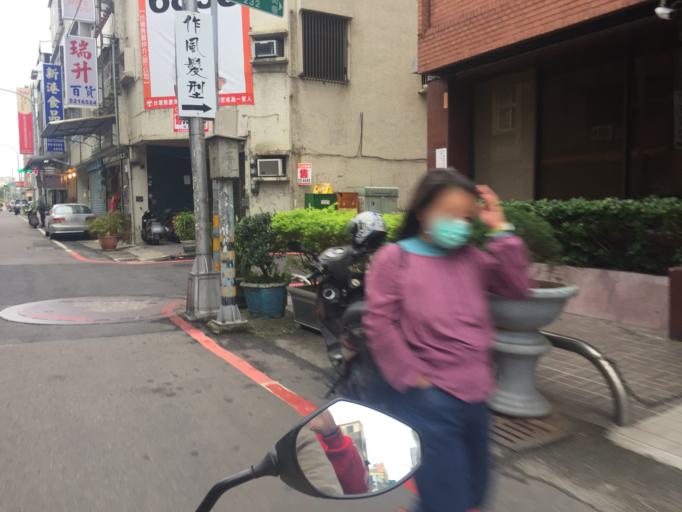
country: TW
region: Taiwan
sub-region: Hsinchu
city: Hsinchu
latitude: 24.7999
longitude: 120.9609
